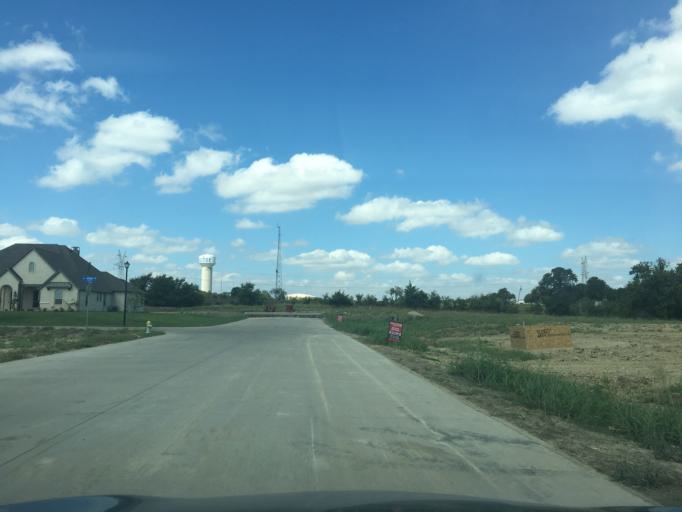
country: US
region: Texas
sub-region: Dallas County
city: Sachse
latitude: 32.9693
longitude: -96.5552
